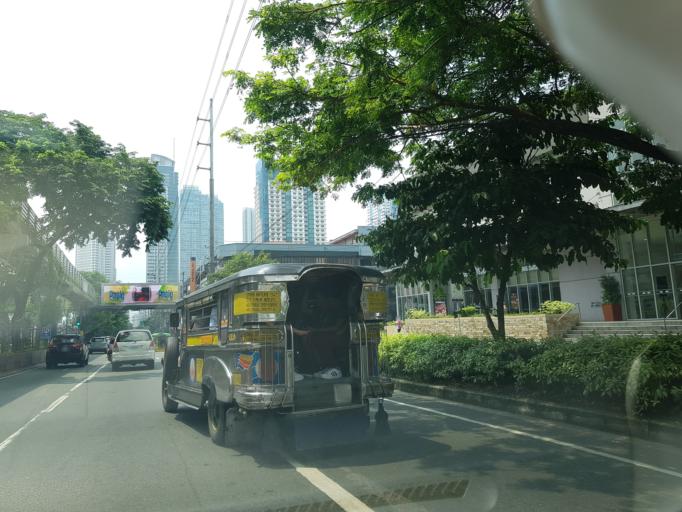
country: PH
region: Metro Manila
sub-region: Pasig
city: Pasig City
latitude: 14.5746
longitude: 121.0615
